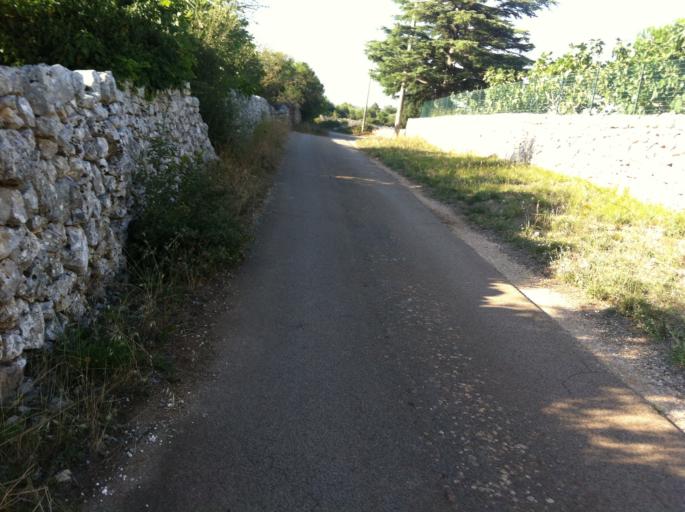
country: IT
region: Apulia
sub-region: Provincia di Bari
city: Noci
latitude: 40.8227
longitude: 17.1398
